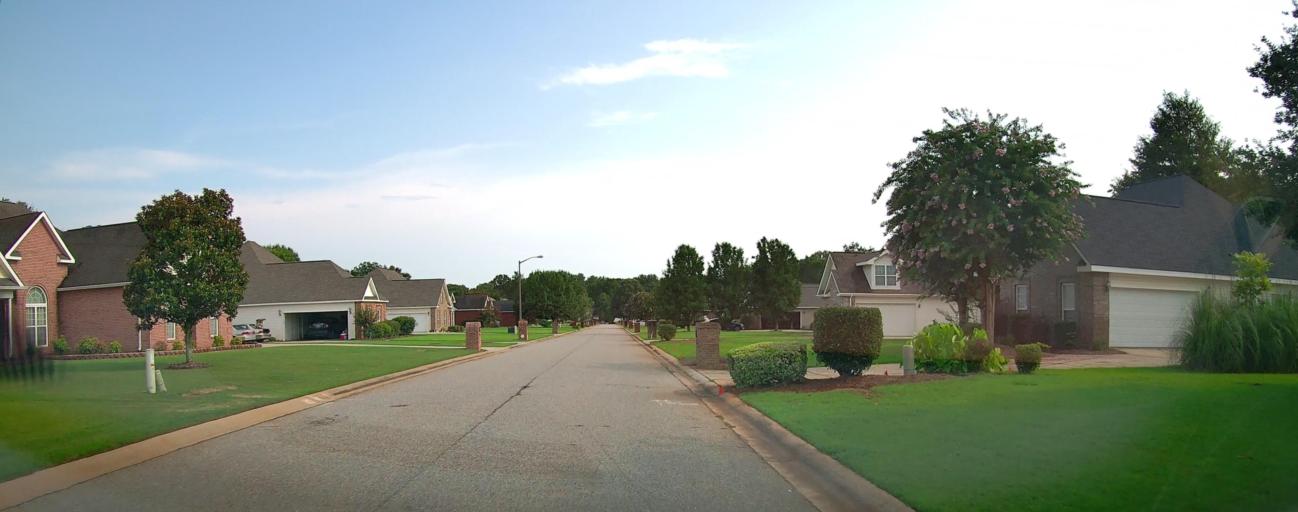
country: US
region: Georgia
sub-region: Houston County
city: Centerville
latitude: 32.6414
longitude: -83.7130
